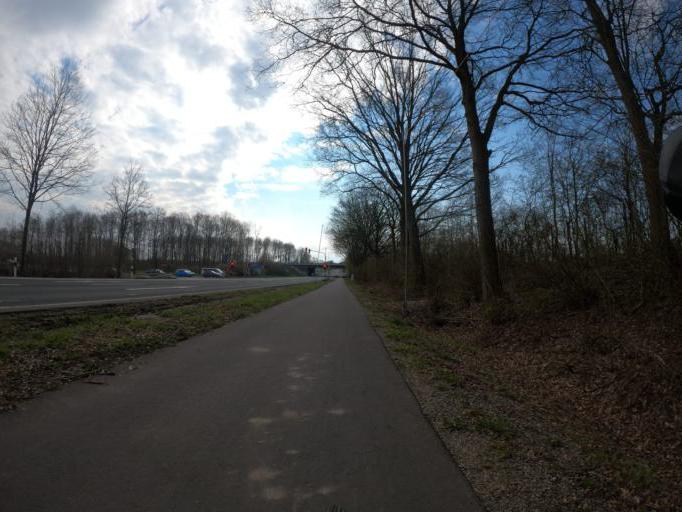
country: BE
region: Wallonia
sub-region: Province de Liege
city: Raeren
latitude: 50.7222
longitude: 6.1237
